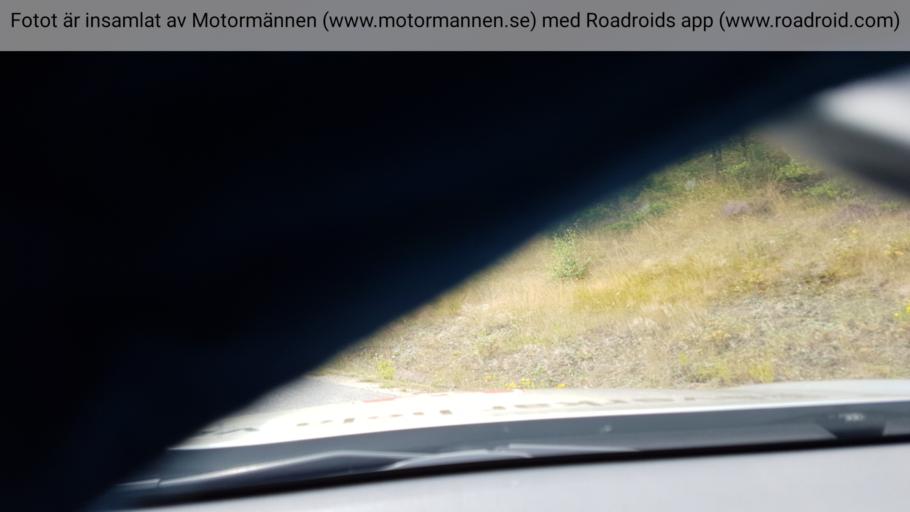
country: SE
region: Vaestra Goetaland
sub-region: Tanums Kommun
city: Tanumshede
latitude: 58.5945
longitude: 11.4540
